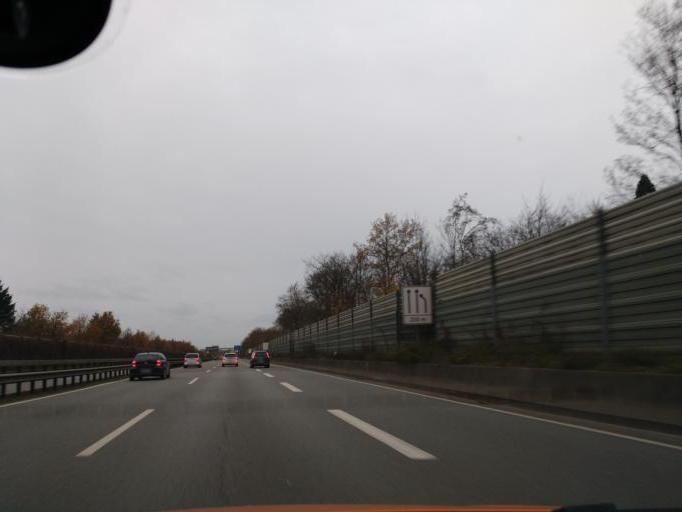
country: DE
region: Lower Saxony
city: Delmenhorst
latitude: 53.0315
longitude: 8.6520
